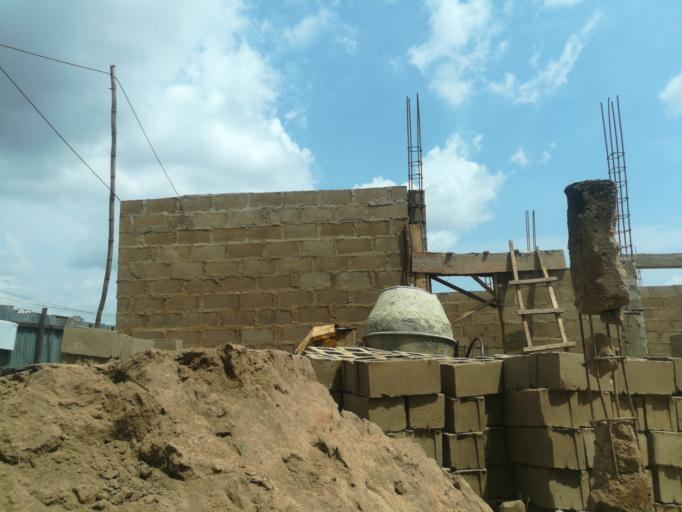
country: NG
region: Oyo
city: Ibadan
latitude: 7.4034
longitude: 3.9334
